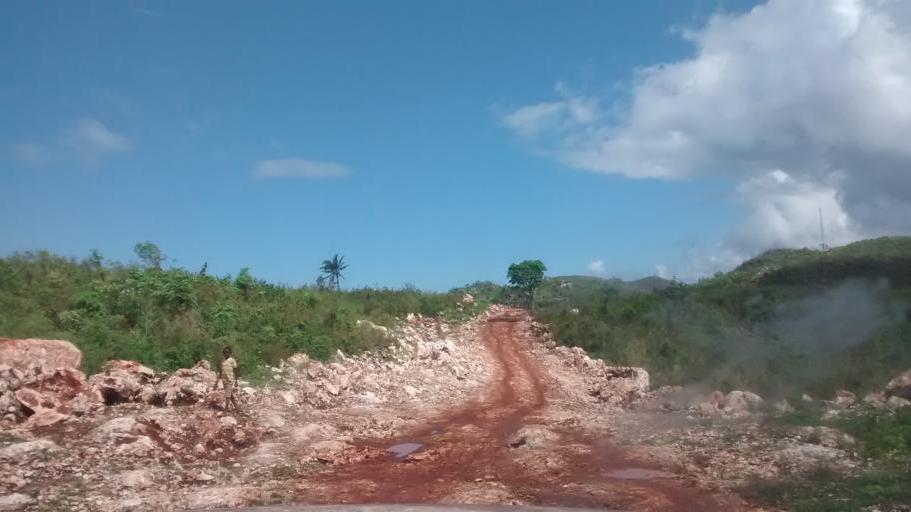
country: HT
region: Grandans
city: Corail
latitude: 18.5393
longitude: -73.9250
